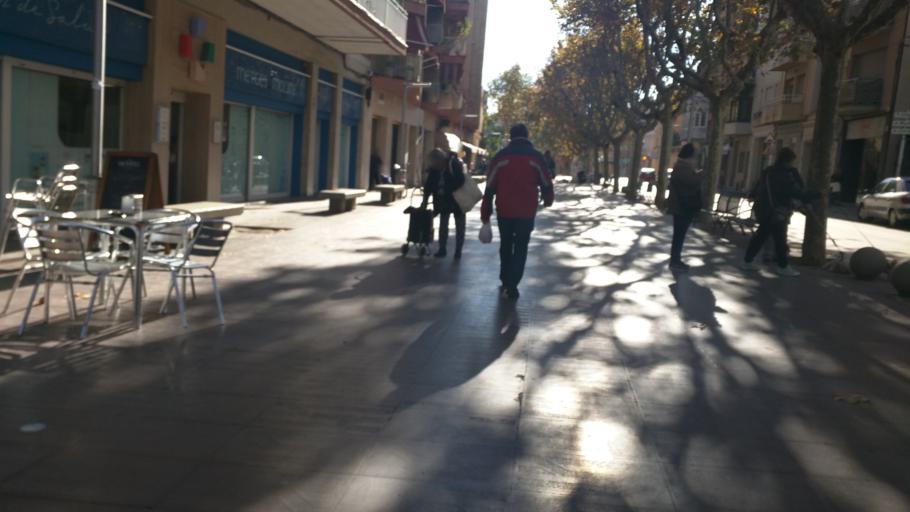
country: ES
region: Catalonia
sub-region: Provincia de Barcelona
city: Molins de Rei
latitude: 41.4108
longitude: 2.0164
